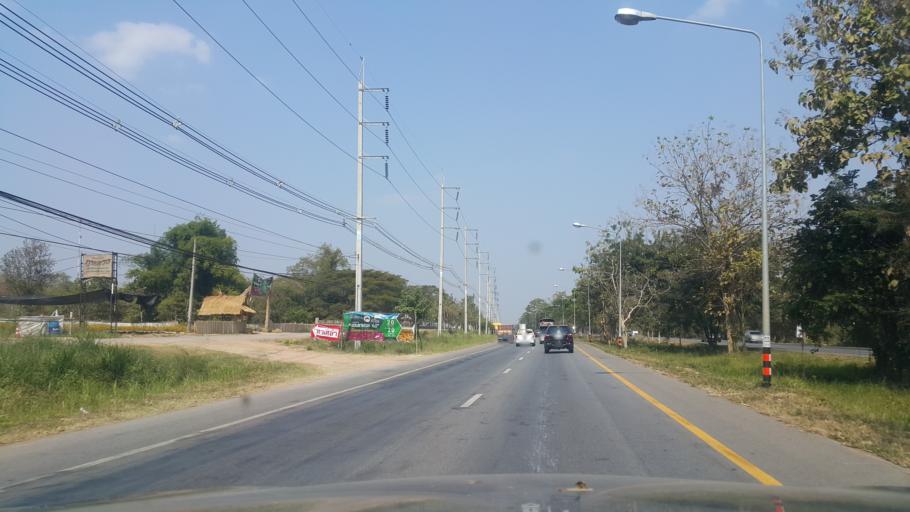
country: TH
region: Nakhon Ratchasima
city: Pak Thong Chai
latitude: 14.5918
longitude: 102.0000
